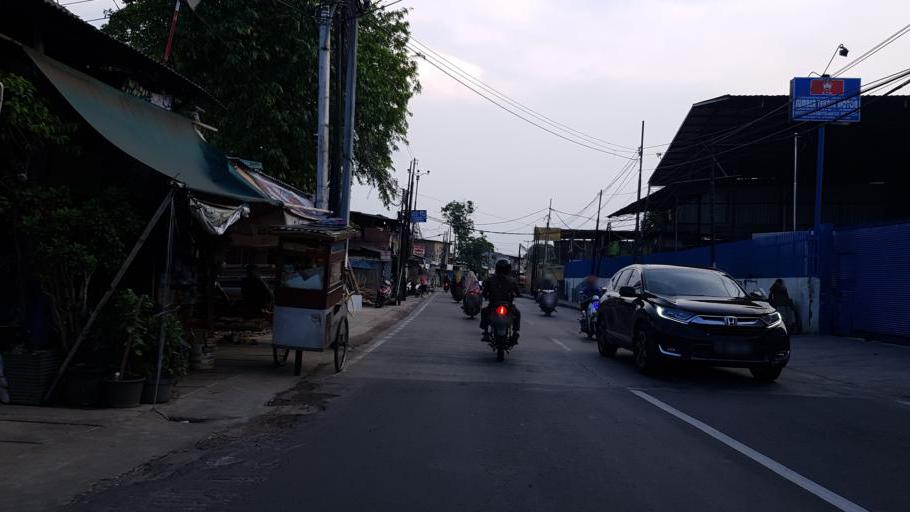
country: ID
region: Jakarta Raya
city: Jakarta
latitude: -6.1395
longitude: 106.7754
